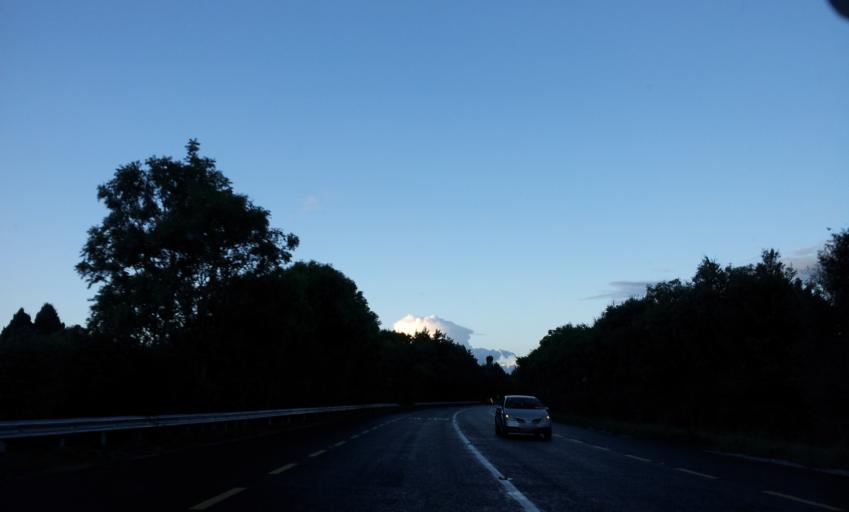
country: IE
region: Munster
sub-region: County Limerick
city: Rathkeale
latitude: 52.5073
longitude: -8.9902
